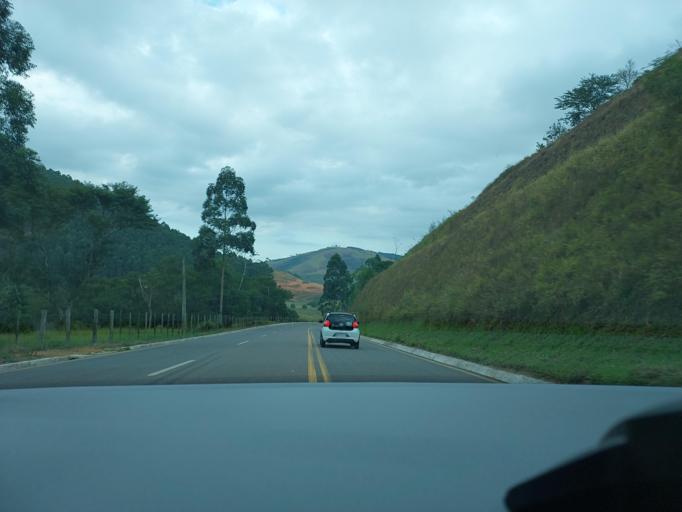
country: BR
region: Minas Gerais
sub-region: Mirai
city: Mirai
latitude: -20.9707
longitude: -42.5909
